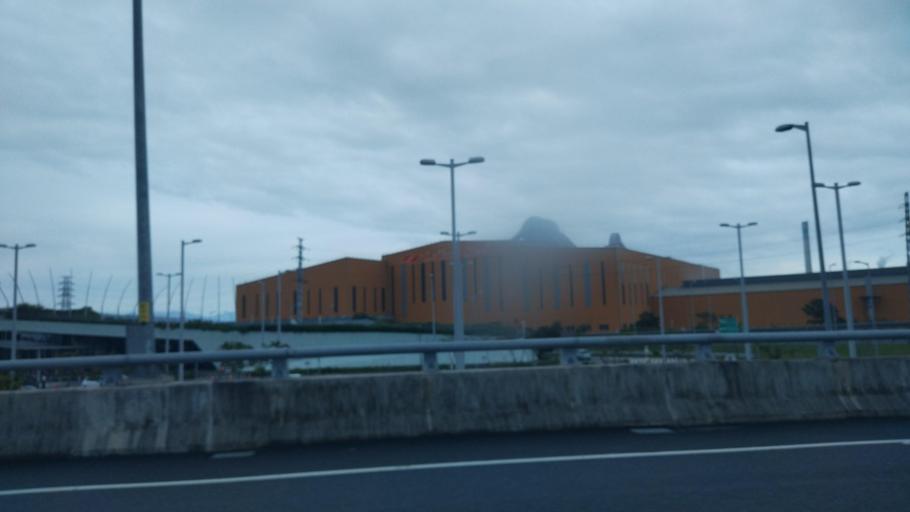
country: TW
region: Taiwan
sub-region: Yilan
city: Yilan
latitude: 24.6212
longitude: 121.8173
